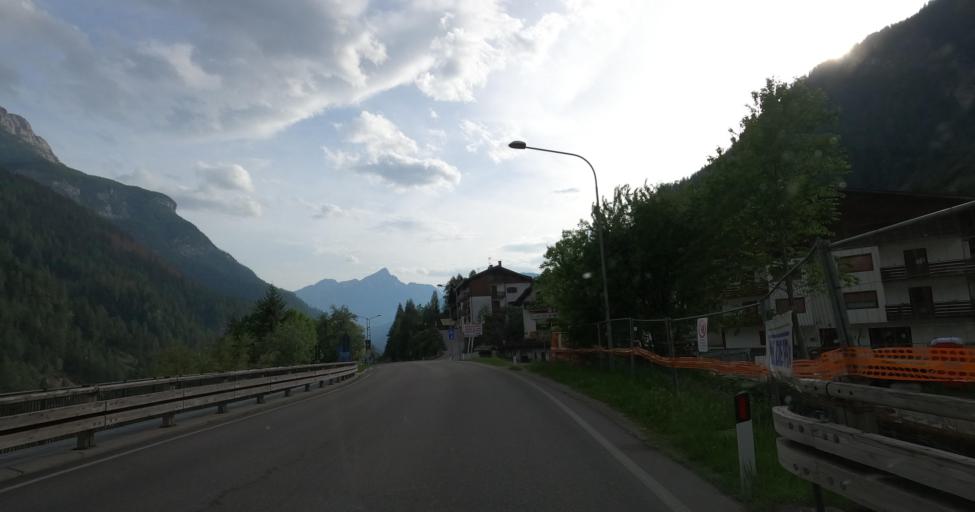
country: IT
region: Veneto
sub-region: Provincia di Belluno
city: Alleghe
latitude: 46.3978
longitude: 12.0125
